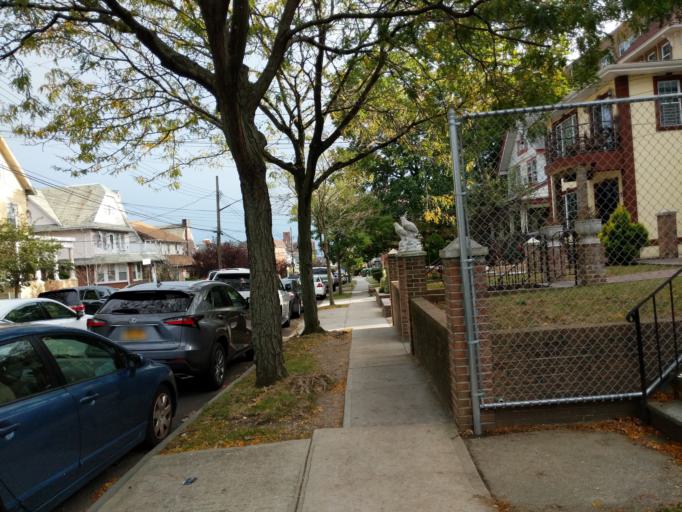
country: US
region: New York
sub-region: Queens County
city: Jamaica
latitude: 40.7124
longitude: -73.7970
